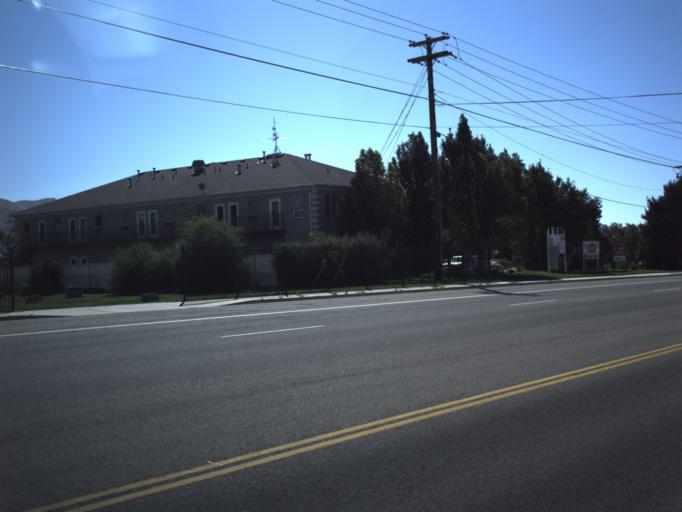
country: US
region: Utah
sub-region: Salt Lake County
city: Bluffdale
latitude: 40.4930
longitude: -111.9389
